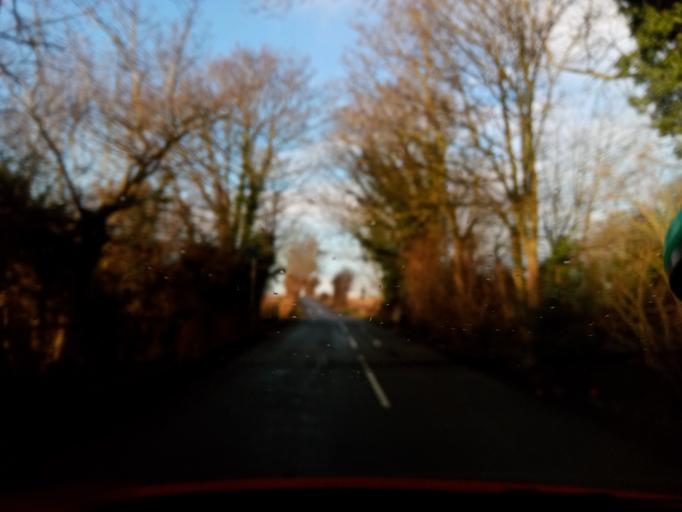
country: GB
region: England
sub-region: Derbyshire
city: Melbourne
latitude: 52.8516
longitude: -1.4289
